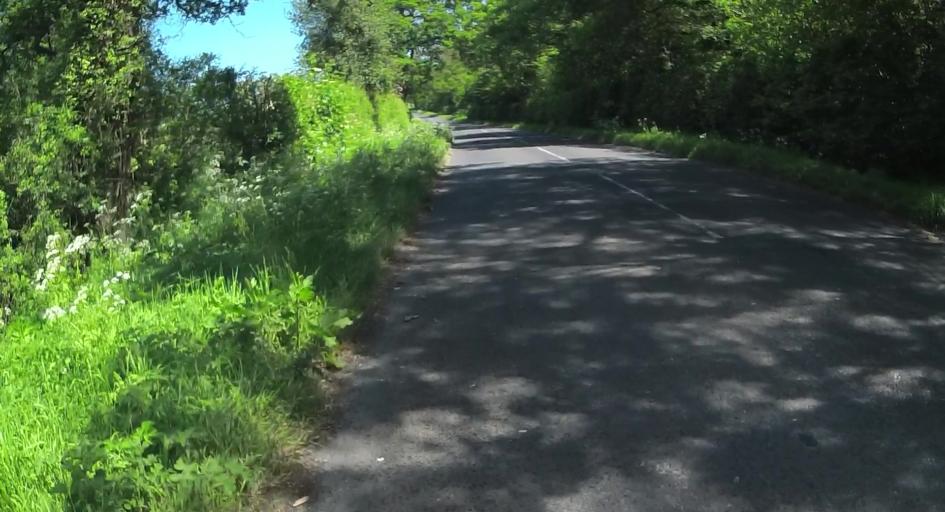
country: GB
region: England
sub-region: Wokingham
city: Swallowfield
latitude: 51.3600
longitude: -0.9819
